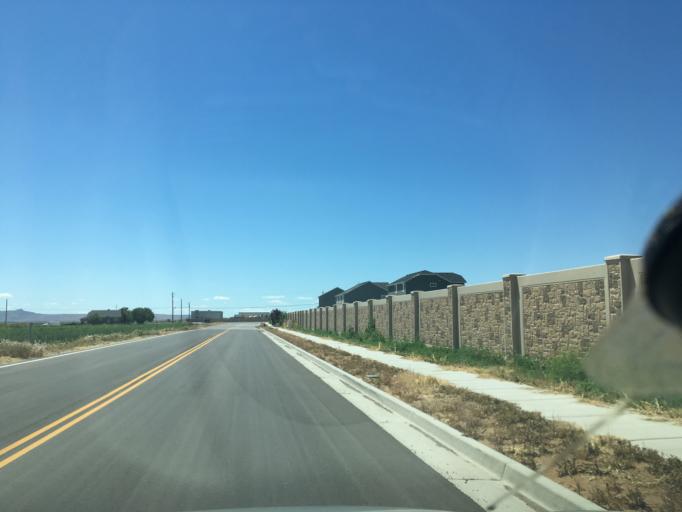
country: US
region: Utah
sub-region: Davis County
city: Layton
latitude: 41.0494
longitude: -112.0041
